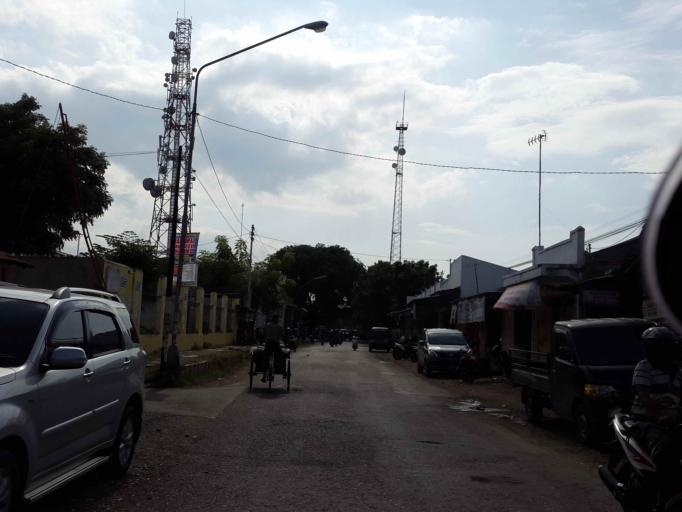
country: ID
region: Central Java
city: Pemalang
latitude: -6.8879
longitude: 109.3905
